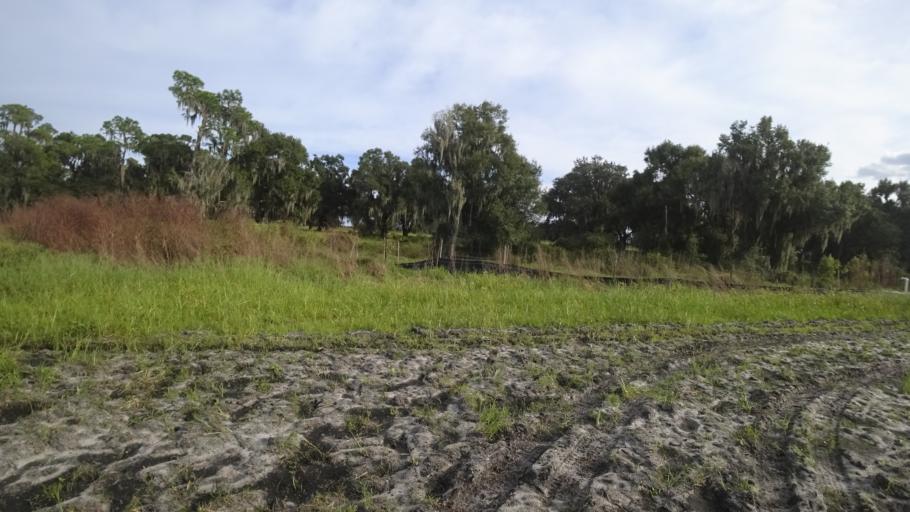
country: US
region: Florida
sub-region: Hillsborough County
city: Wimauma
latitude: 27.5535
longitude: -82.0927
